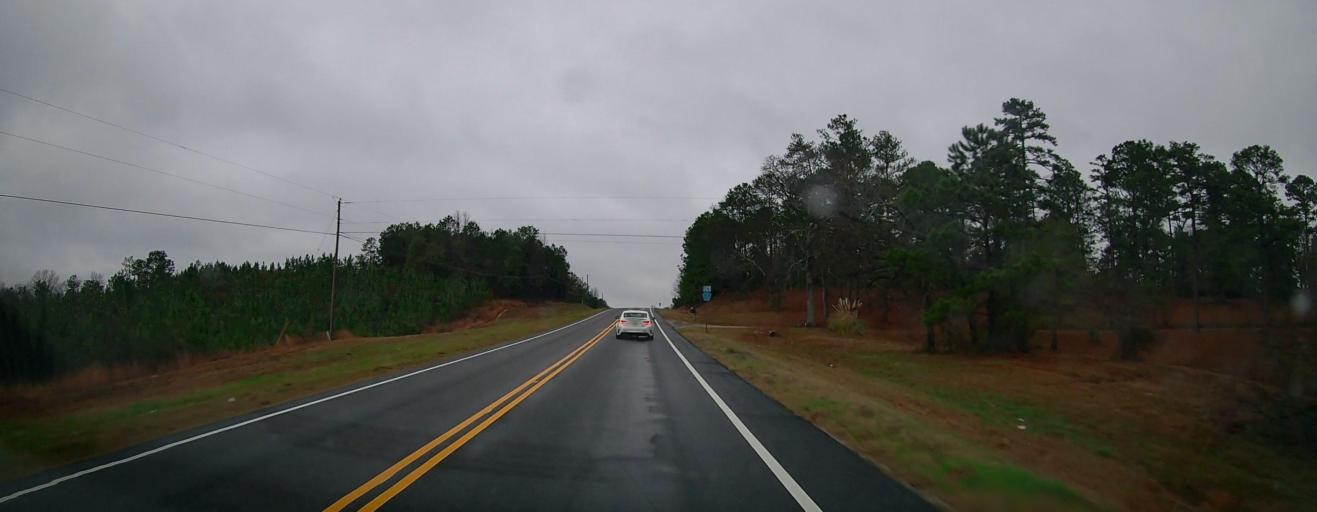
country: US
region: Alabama
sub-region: Chilton County
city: Clanton
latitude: 32.6882
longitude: -86.7935
